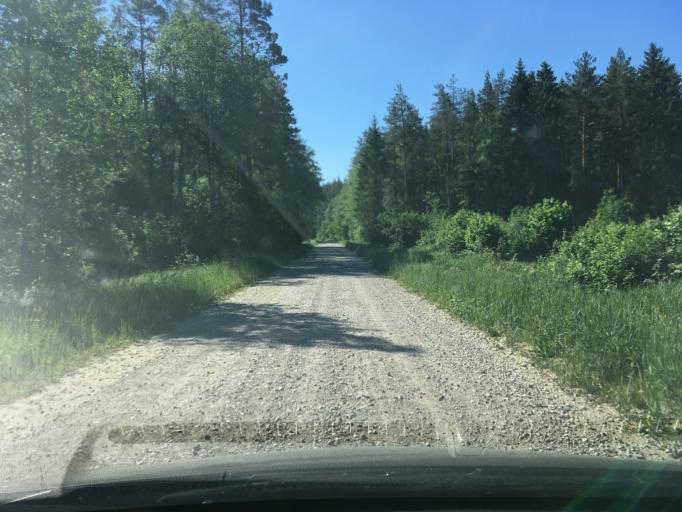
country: EE
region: Laeaene
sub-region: Lihula vald
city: Lihula
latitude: 58.6405
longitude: 23.7902
